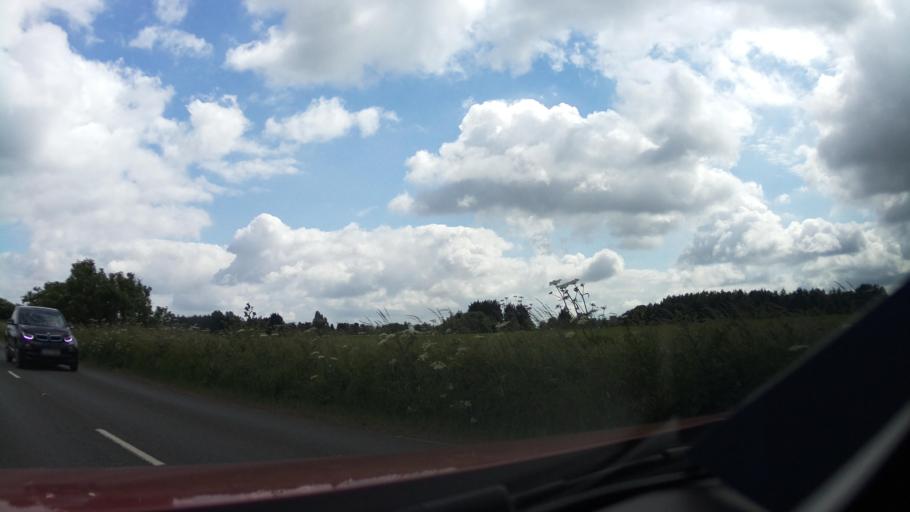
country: GB
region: England
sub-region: South Gloucestershire
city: Cold Ashton
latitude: 51.4244
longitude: -2.4003
